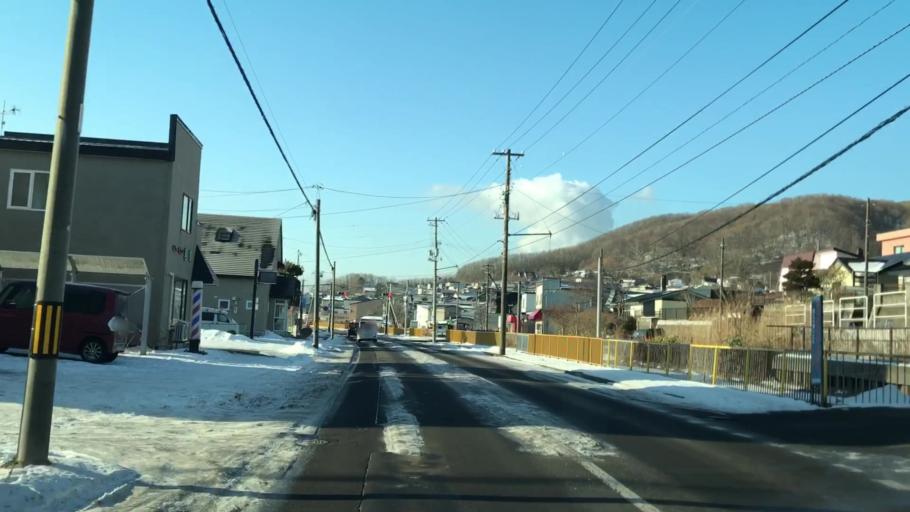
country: JP
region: Hokkaido
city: Muroran
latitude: 42.3714
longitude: 141.0534
